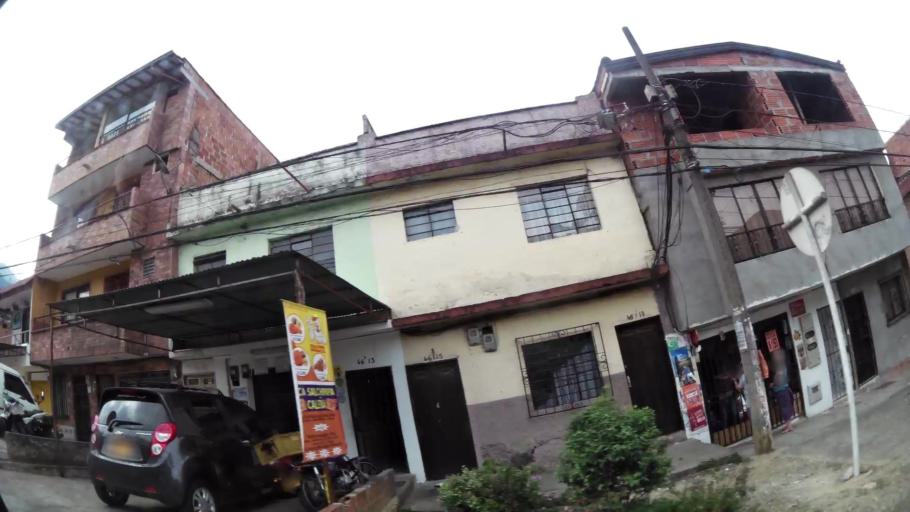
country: CO
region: Antioquia
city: Medellin
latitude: 6.2832
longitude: -75.5545
